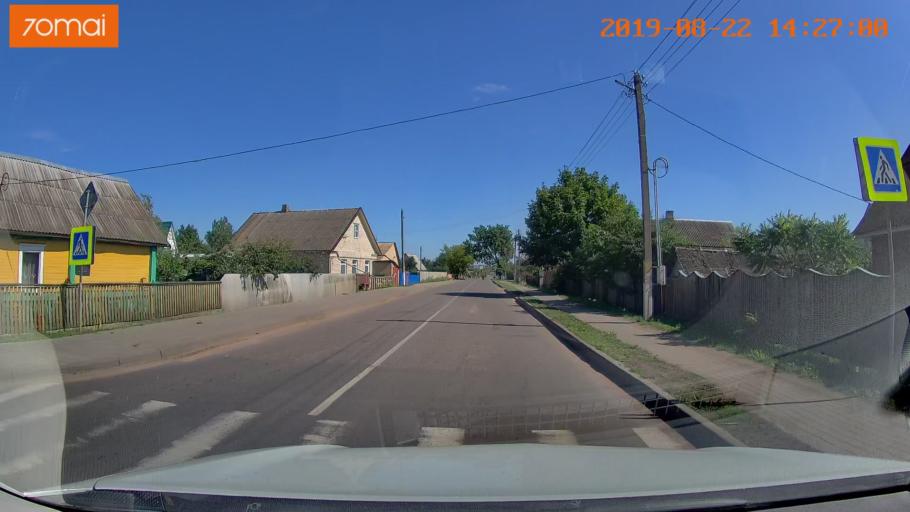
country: BY
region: Mogilev
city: Asipovichy
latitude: 53.2979
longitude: 28.6206
